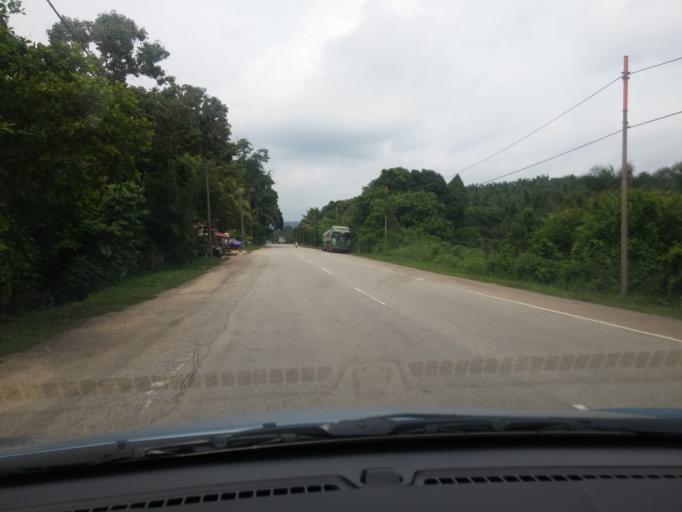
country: MY
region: Pahang
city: Kuantan
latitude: 3.8839
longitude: 103.1611
